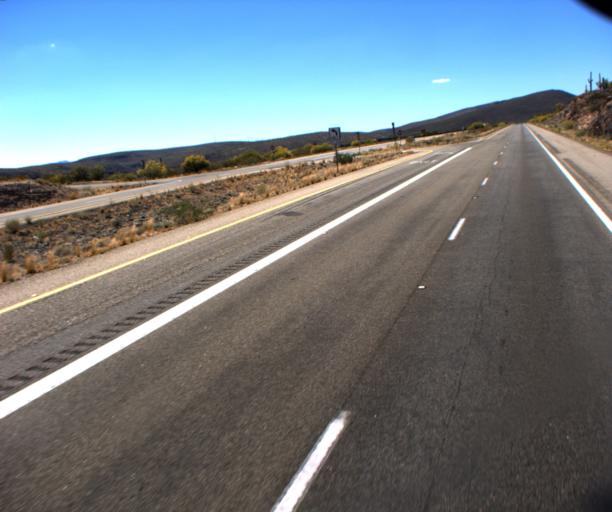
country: US
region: Arizona
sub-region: Yavapai County
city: Bagdad
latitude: 34.5331
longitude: -113.4318
